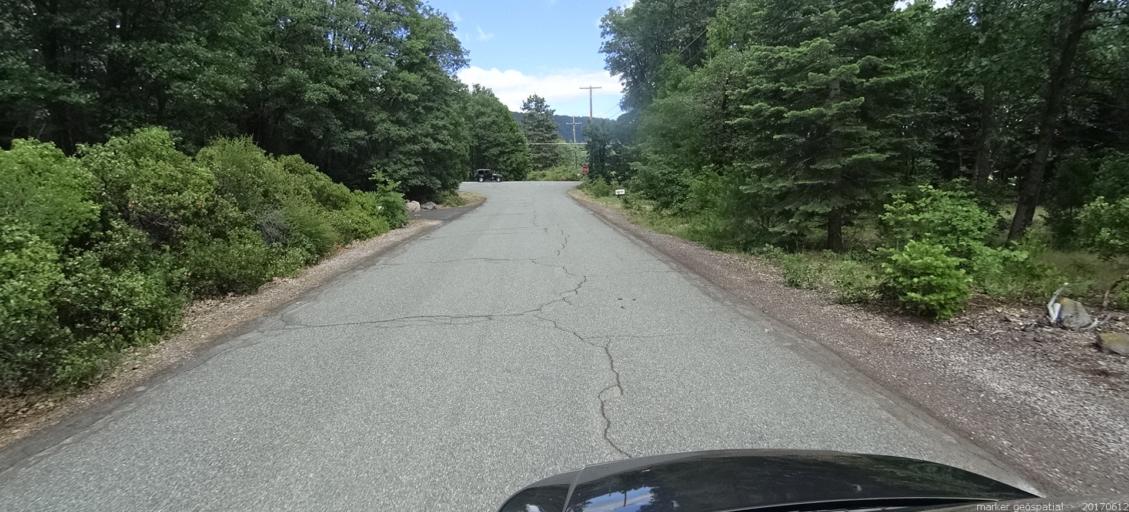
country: US
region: California
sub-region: Siskiyou County
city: Mount Shasta
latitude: 41.3246
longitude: -122.3072
